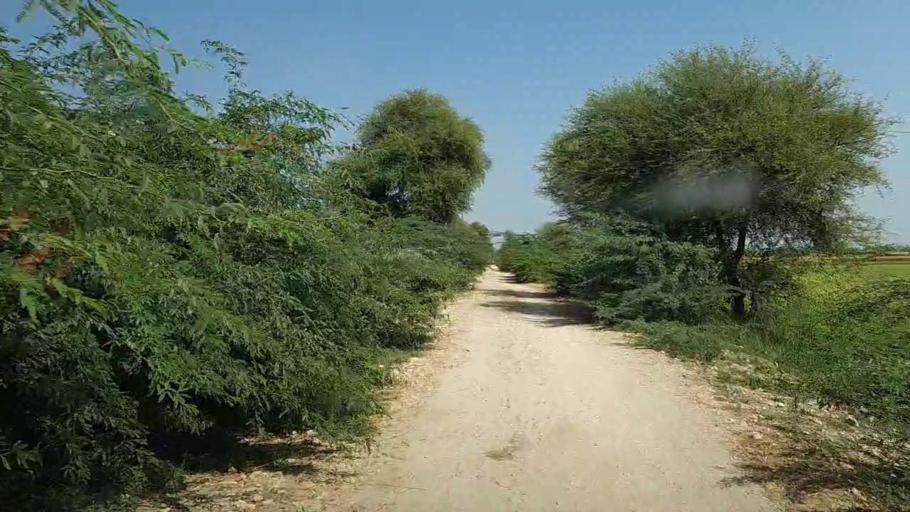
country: PK
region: Sindh
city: Mirpur Batoro
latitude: 24.7132
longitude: 68.4311
